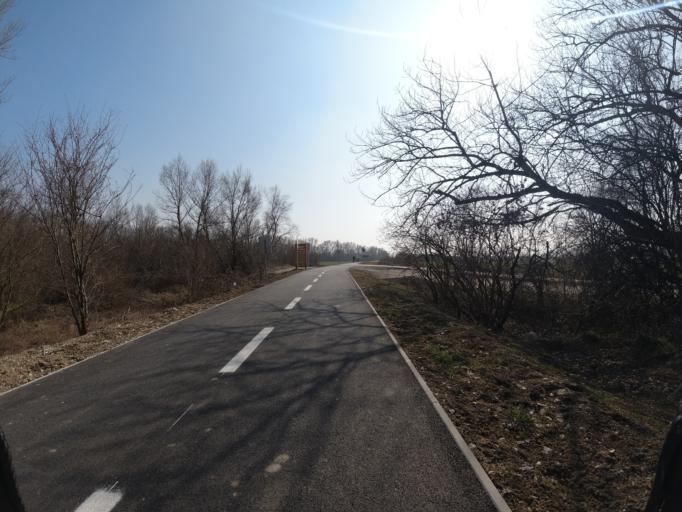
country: SK
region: Trenciansky
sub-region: Okres Nove Mesto nad Vahom
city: Nove Mesto nad Vahom
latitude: 48.7473
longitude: 17.8504
